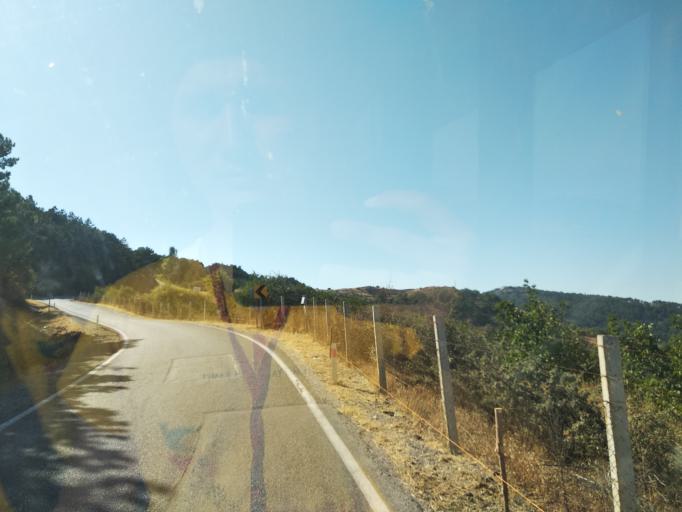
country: TR
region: Izmir
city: Gaziemir
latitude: 38.3195
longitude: 27.0116
